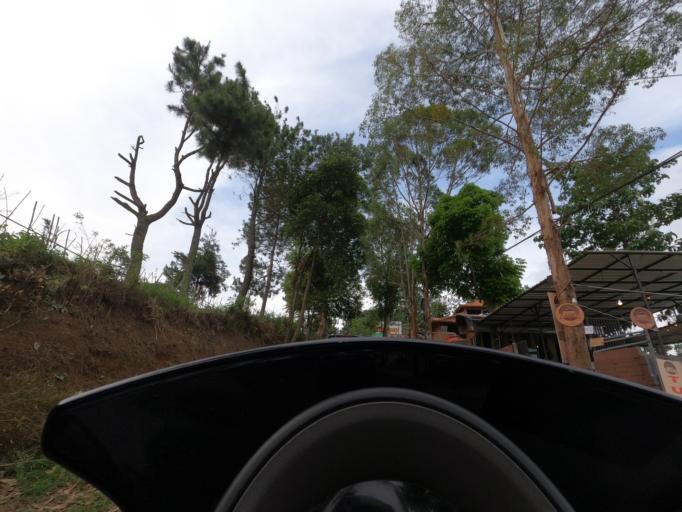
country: ID
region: West Java
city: Lembang
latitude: -6.8311
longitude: 107.6236
